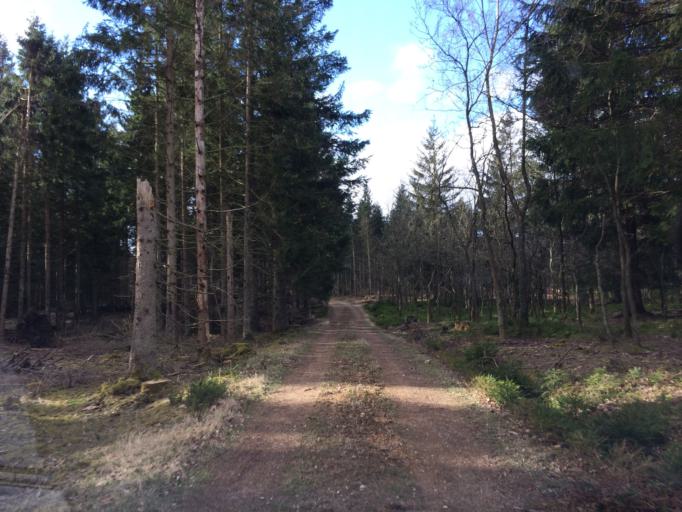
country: DK
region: Central Jutland
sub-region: Holstebro Kommune
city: Ulfborg
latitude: 56.2743
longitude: 8.4467
